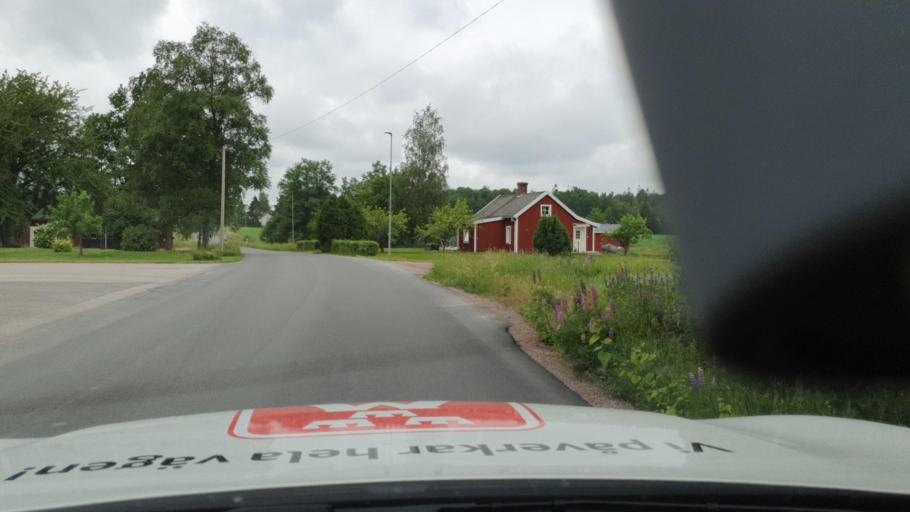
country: SE
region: Vaestra Goetaland
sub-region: Tibro Kommun
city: Tibro
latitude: 58.4067
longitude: 14.1720
